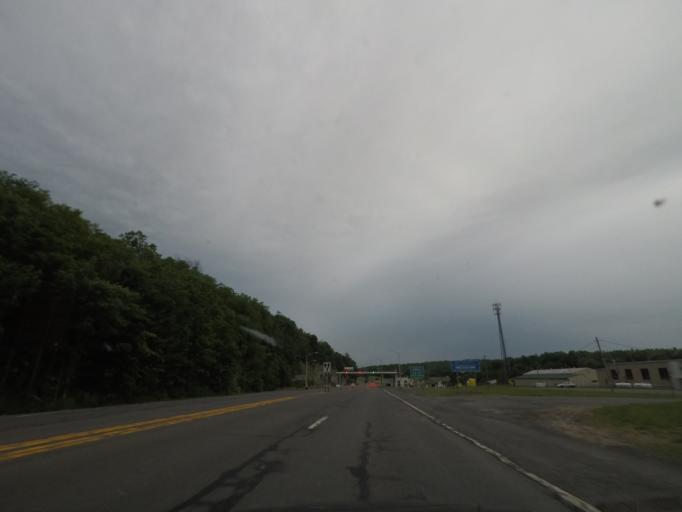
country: US
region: New York
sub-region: Columbia County
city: Chatham
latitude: 42.4163
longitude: -73.5488
